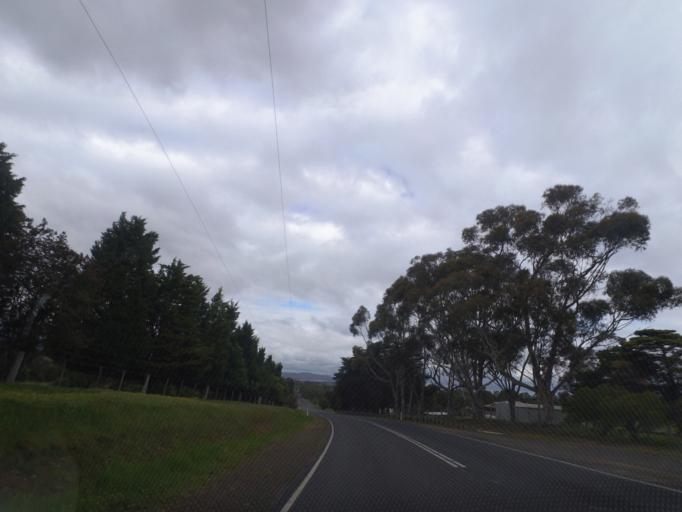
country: AU
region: Victoria
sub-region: Whittlesea
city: Whittlesea
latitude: -37.4930
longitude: 145.0643
